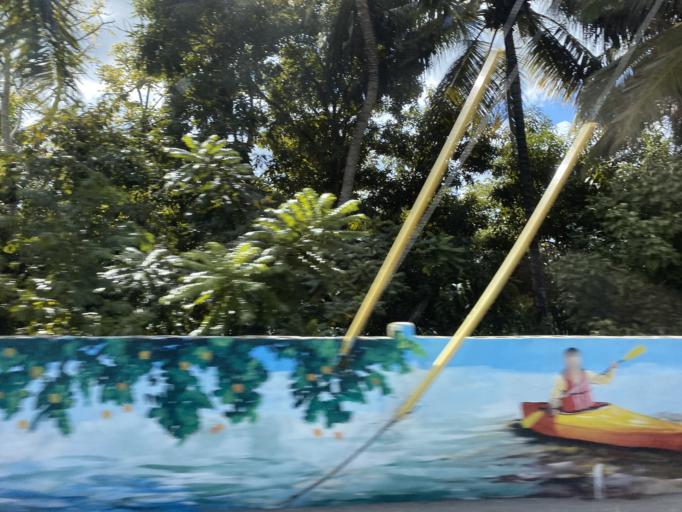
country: DO
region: Espaillat
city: Jamao al Norte
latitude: 19.6722
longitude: -70.3727
